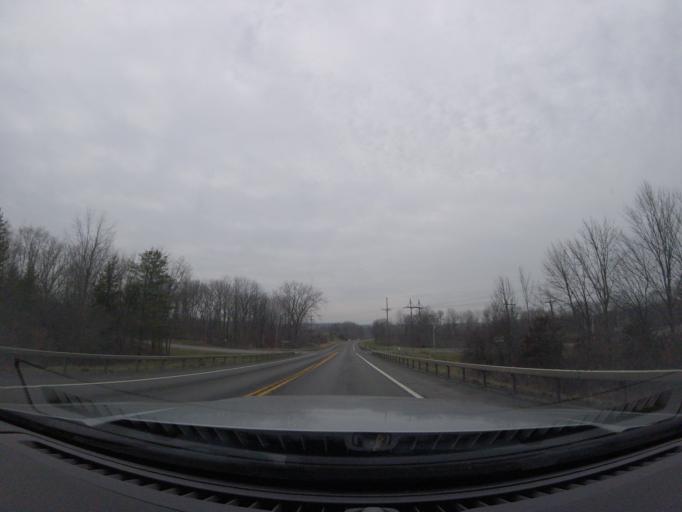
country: US
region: New York
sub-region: Yates County
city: Penn Yan
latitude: 42.6768
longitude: -76.9556
